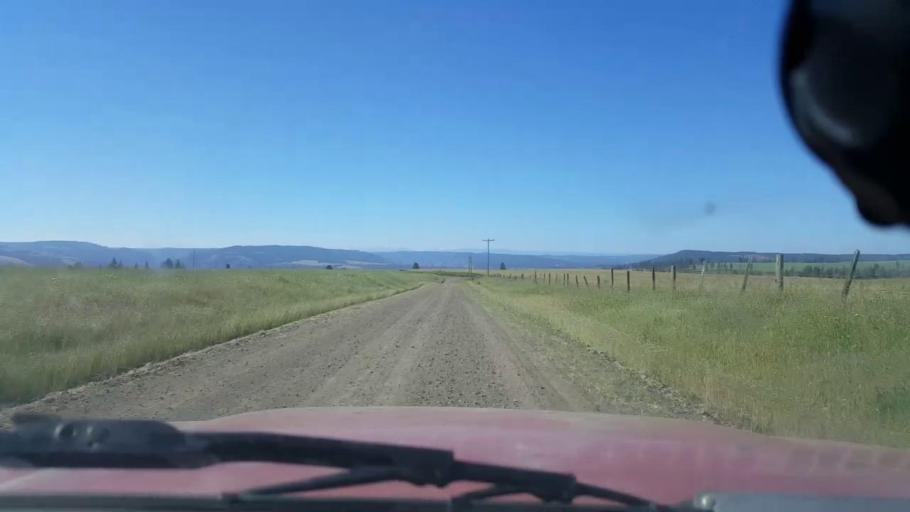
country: US
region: Washington
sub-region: Garfield County
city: Pomeroy
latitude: 45.9871
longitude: -117.4581
